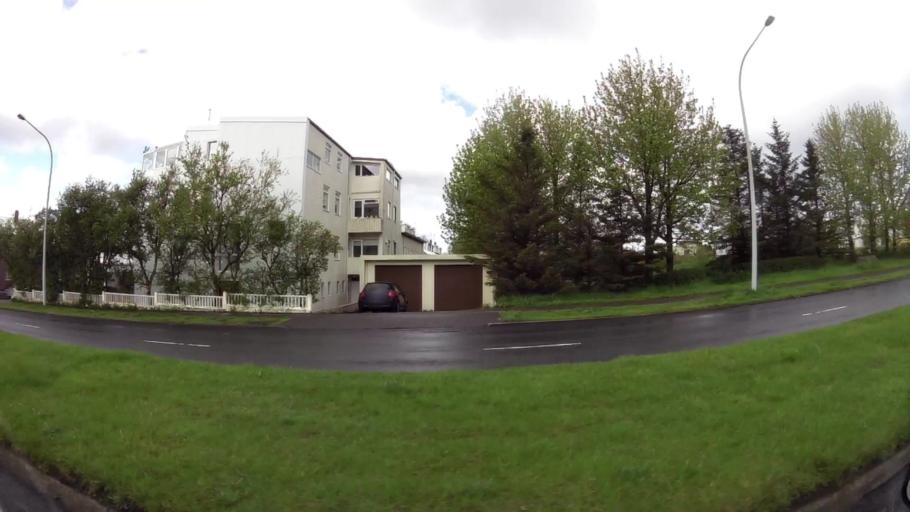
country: IS
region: Capital Region
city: Seltjarnarnes
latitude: 64.1361
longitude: -21.9558
